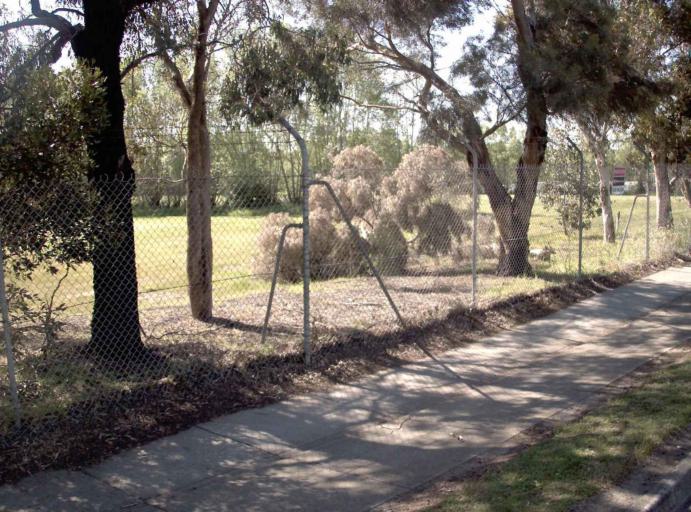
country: AU
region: Victoria
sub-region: Knox
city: Knoxfield
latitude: -37.8757
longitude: 145.2579
